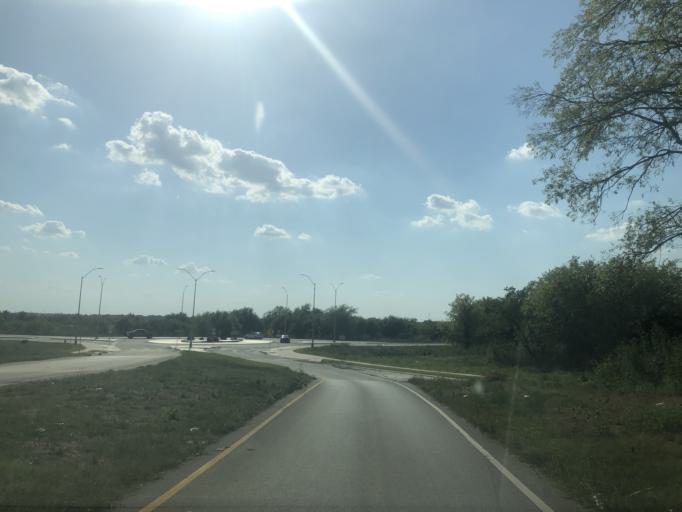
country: US
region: Texas
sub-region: Tarrant County
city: Saginaw
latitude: 32.8480
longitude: -97.3893
